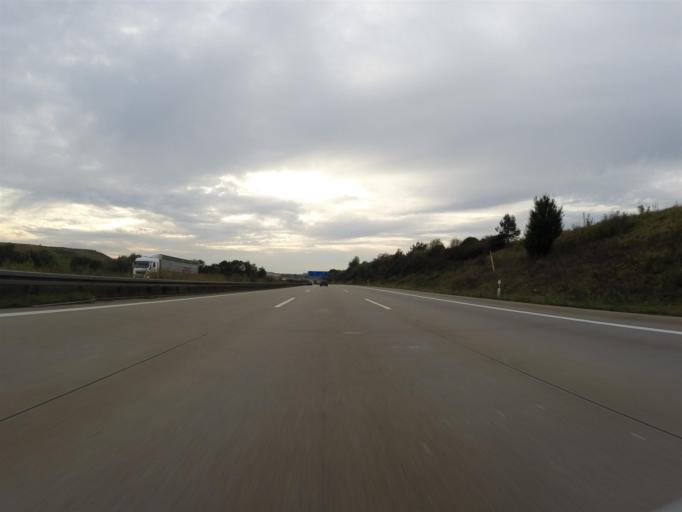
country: DE
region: Saxony
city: Reinsberg
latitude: 51.0586
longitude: 13.3897
